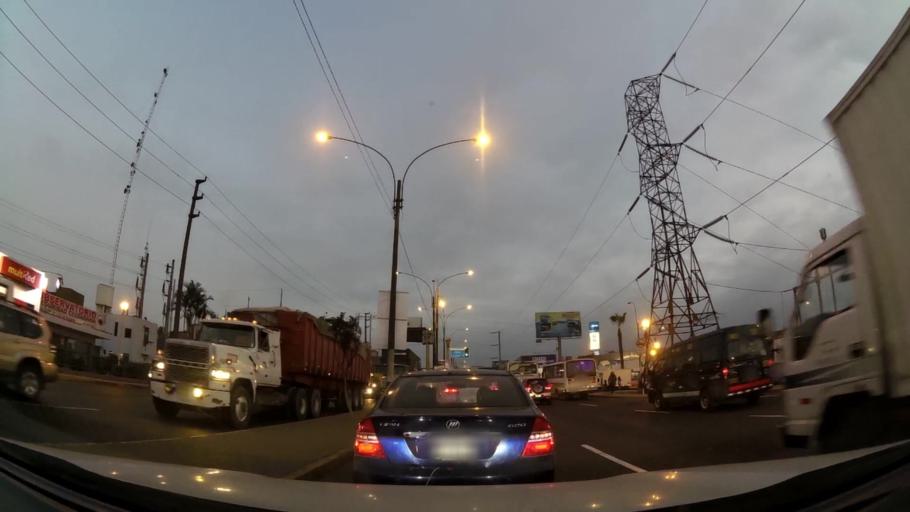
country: PE
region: Callao
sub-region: Callao
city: Callao
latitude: -12.0447
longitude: -77.0987
